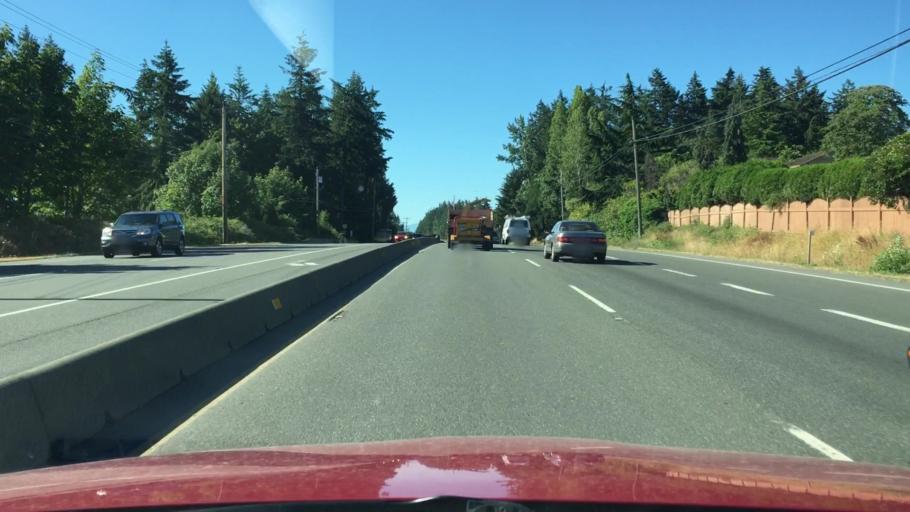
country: CA
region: British Columbia
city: North Saanich
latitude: 48.5523
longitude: -123.3925
